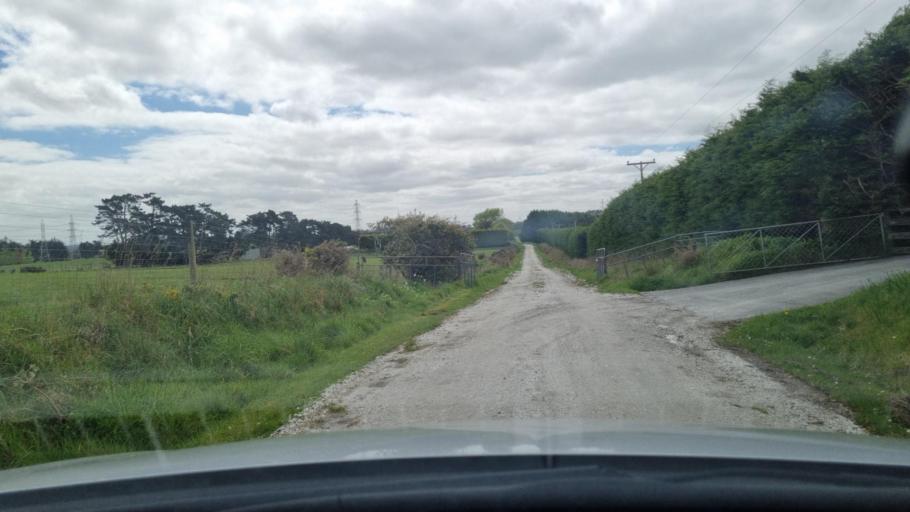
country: NZ
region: Southland
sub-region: Invercargill City
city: Invercargill
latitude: -46.3914
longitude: 168.4053
